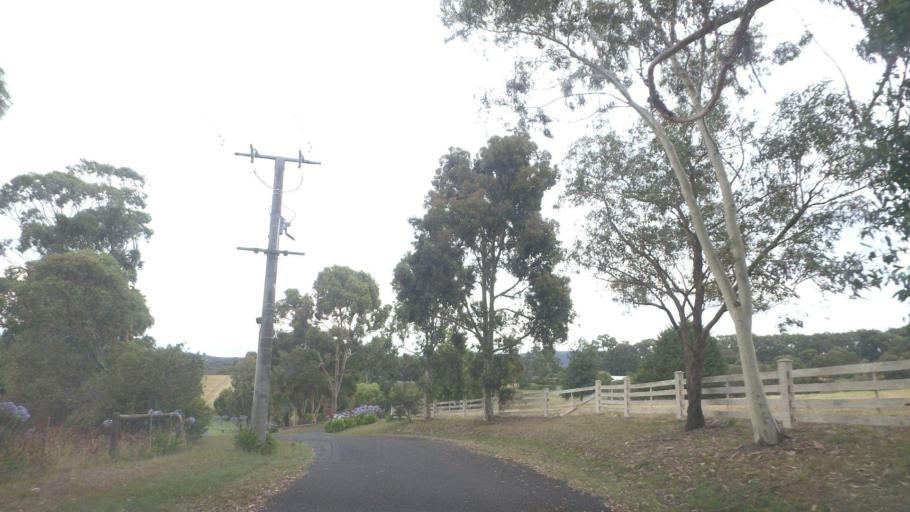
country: AU
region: Victoria
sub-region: Yarra Ranges
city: Mount Evelyn
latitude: -37.7706
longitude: 145.3999
